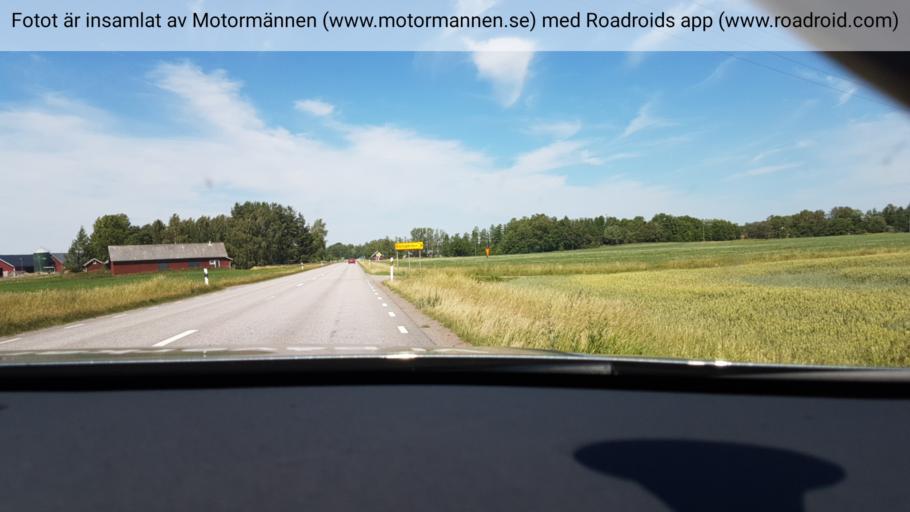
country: SE
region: Vaestra Goetaland
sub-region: Skovde Kommun
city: Stopen
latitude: 58.4836
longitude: 13.9580
